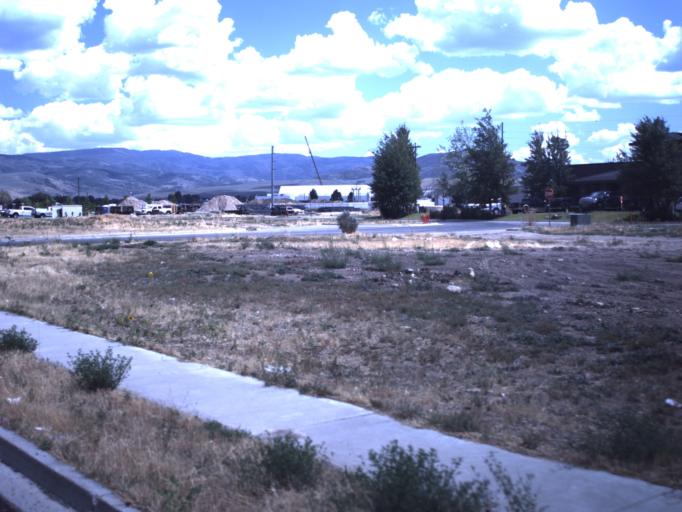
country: US
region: Utah
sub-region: Wasatch County
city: Heber
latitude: 40.4928
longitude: -111.4103
